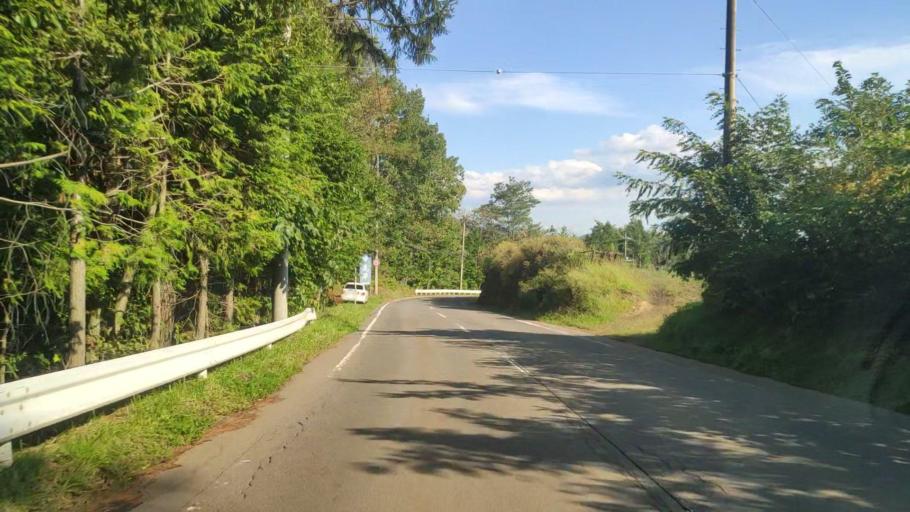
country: JP
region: Nagano
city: Suzaka
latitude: 36.5604
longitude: 138.5584
